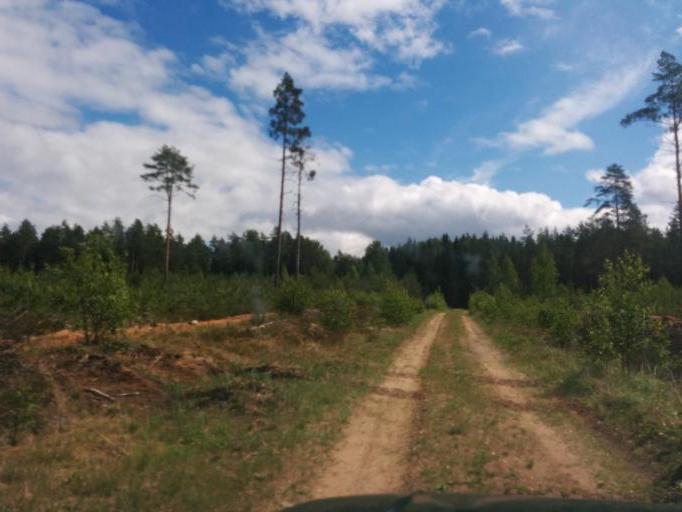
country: LV
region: Vilaka
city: Vilaka
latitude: 57.3334
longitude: 27.6891
